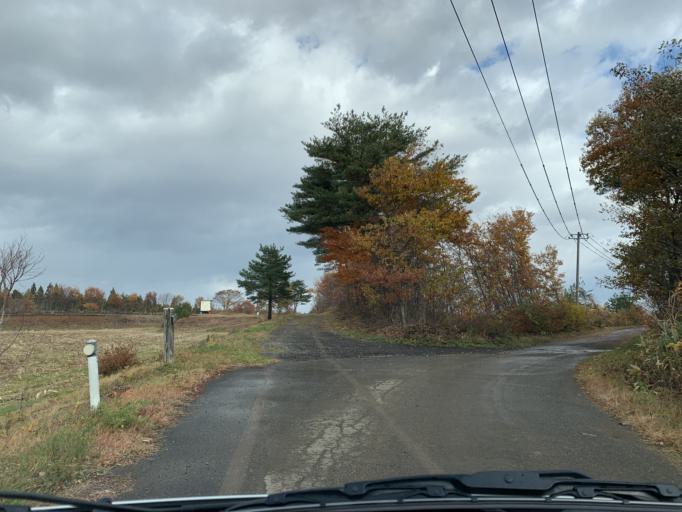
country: JP
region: Iwate
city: Mizusawa
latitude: 39.1038
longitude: 140.9689
